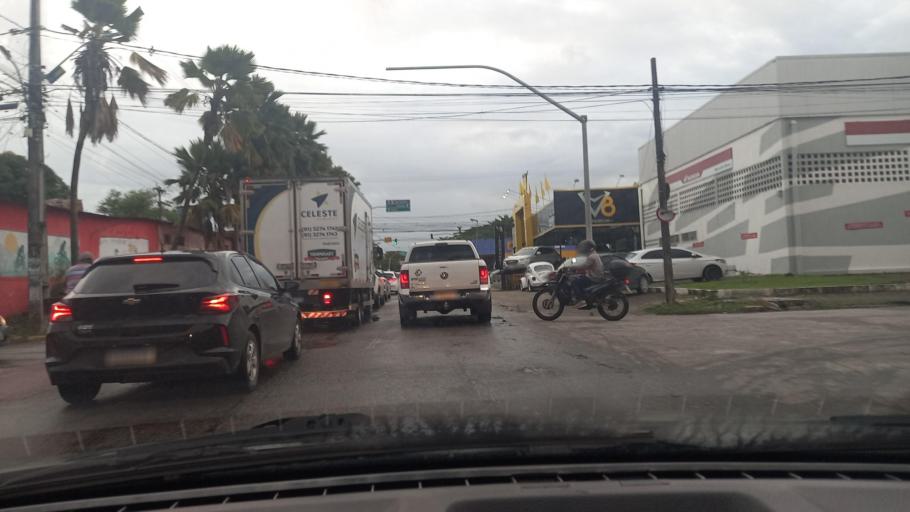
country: ET
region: Gambela
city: Gambela
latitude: 8.1069
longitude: 34.9265
